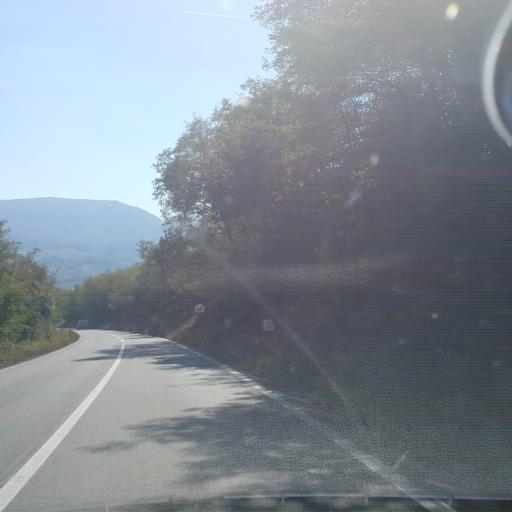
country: RS
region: Central Serbia
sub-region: Nisavski Okrug
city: Svrljig
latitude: 43.4222
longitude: 22.1313
